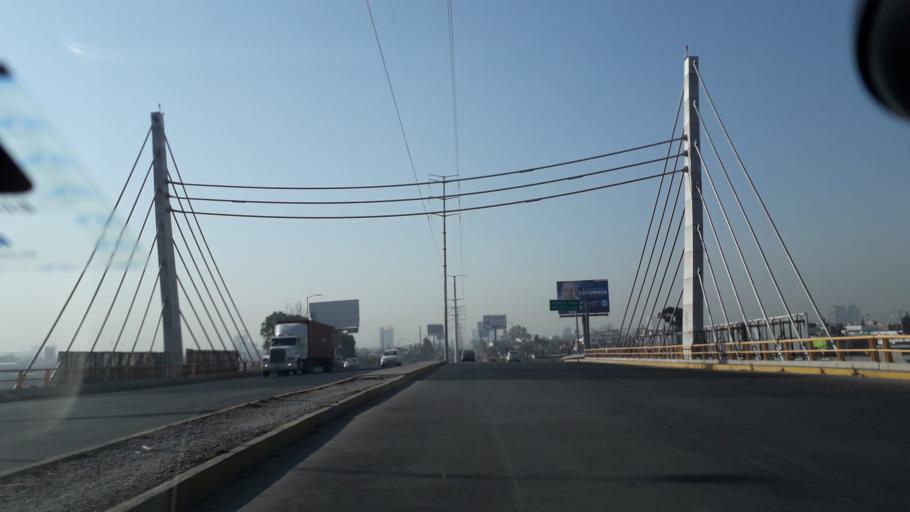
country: MX
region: Puebla
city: Tlazcalancingo
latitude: 19.0360
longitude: -98.2568
